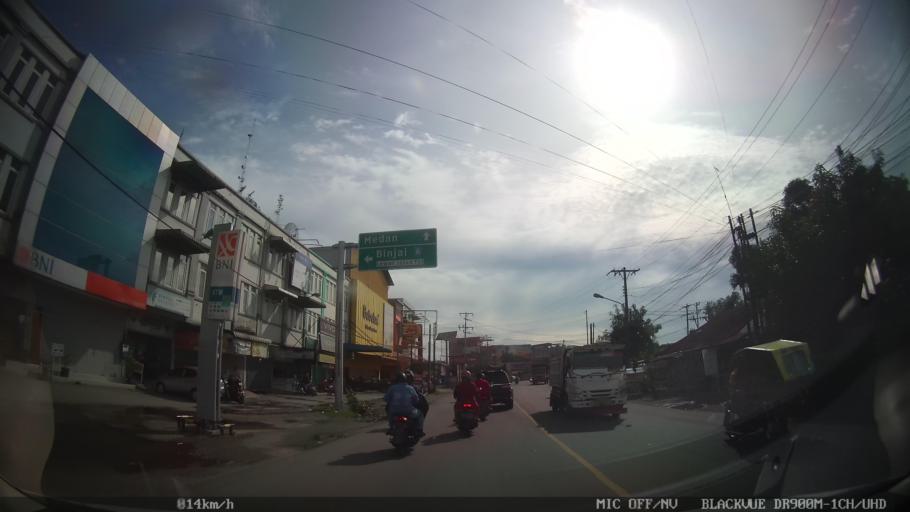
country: ID
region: North Sumatra
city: Medan
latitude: 3.6273
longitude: 98.6616
